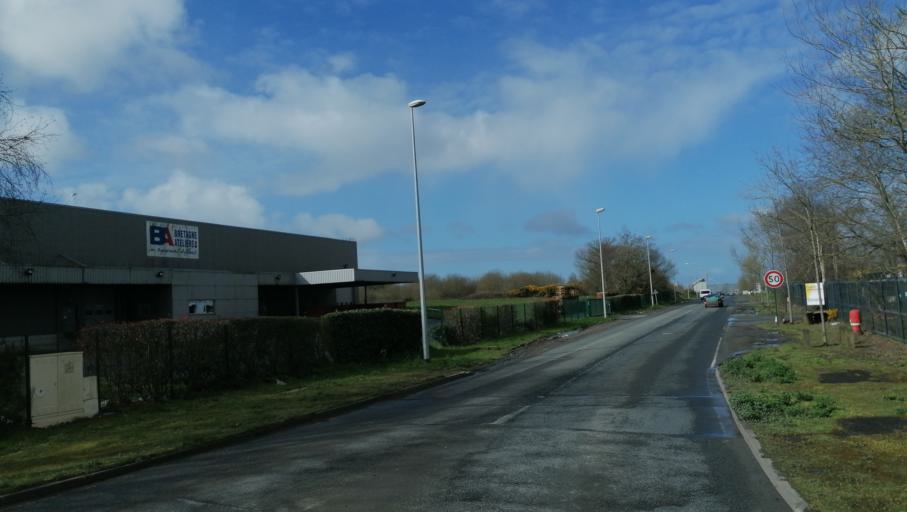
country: FR
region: Brittany
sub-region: Departement des Cotes-d'Armor
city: Saint-Julien
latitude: 48.4610
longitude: -2.7910
